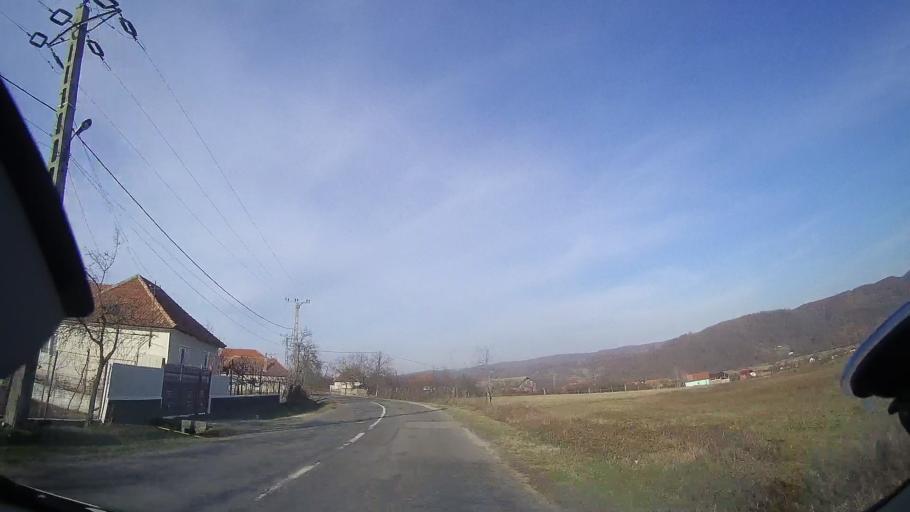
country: RO
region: Bihor
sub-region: Comuna Brusturi
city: Brusturi
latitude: 47.1283
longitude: 22.2709
